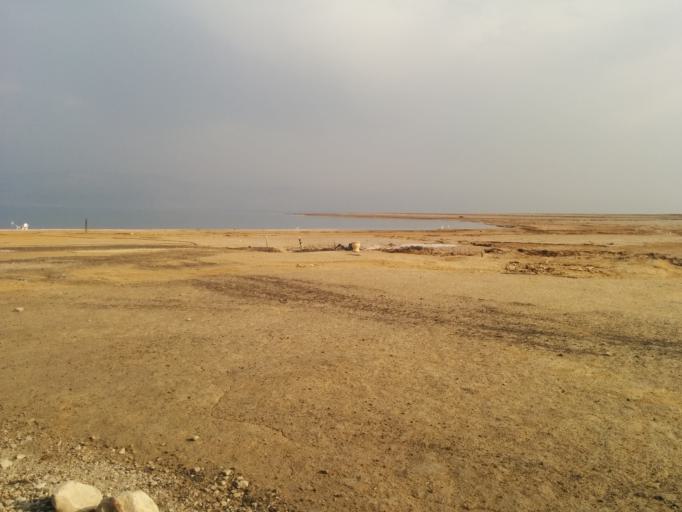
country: PS
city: `Arab ar Rashaydah
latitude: 31.4209
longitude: 35.3911
